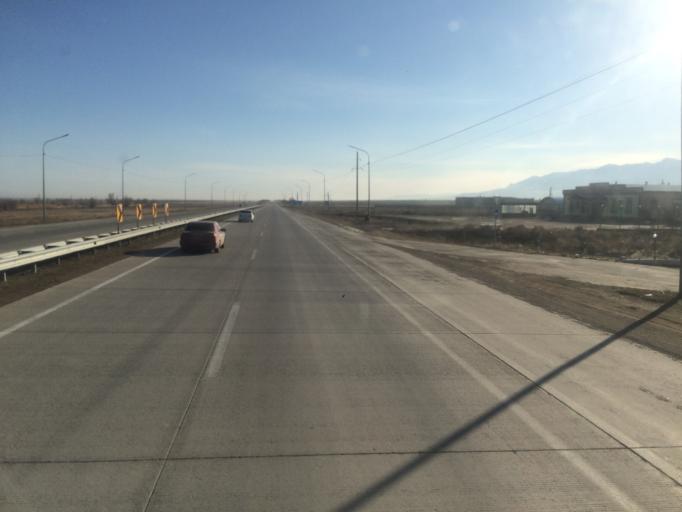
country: KZ
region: Zhambyl
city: Sarykemer
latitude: 43.0086
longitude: 71.8067
